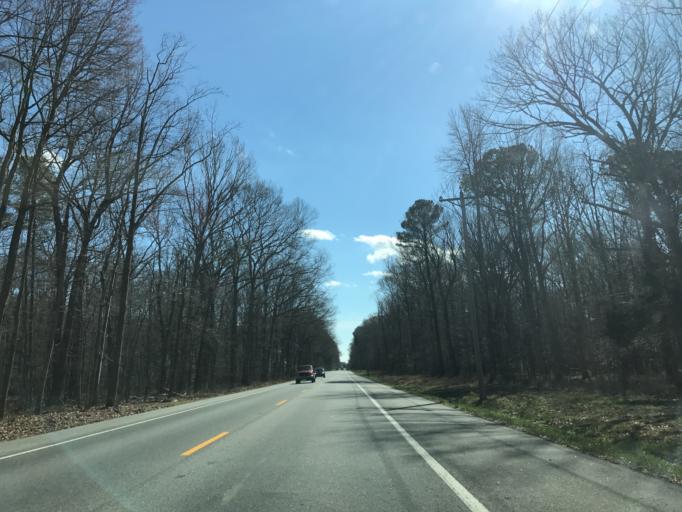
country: US
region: Maryland
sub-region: Kent County
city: Rock Hall
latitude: 39.1932
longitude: -76.1915
